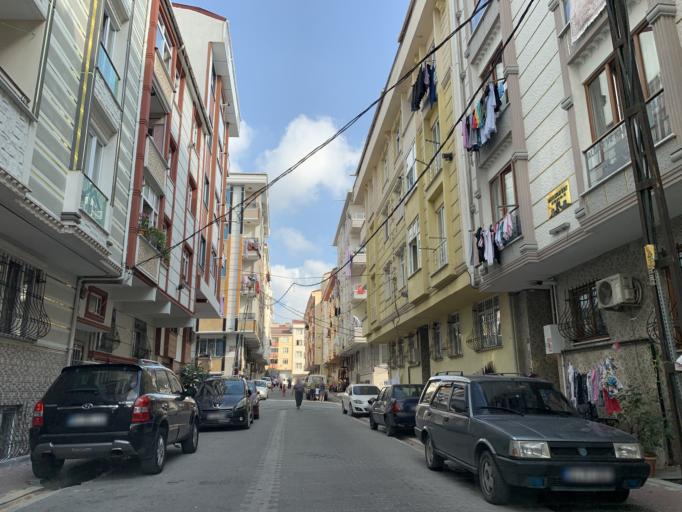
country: TR
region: Istanbul
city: Esenyurt
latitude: 41.0299
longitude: 28.6772
